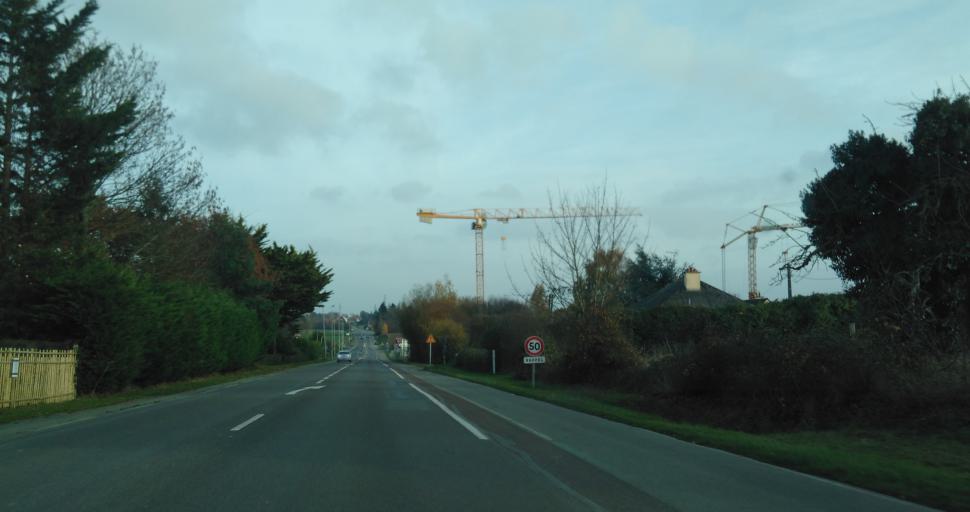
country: FR
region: Brittany
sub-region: Departement d'Ille-et-Vilaine
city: Vezin-le-Coquet
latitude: 48.1188
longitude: -1.7467
